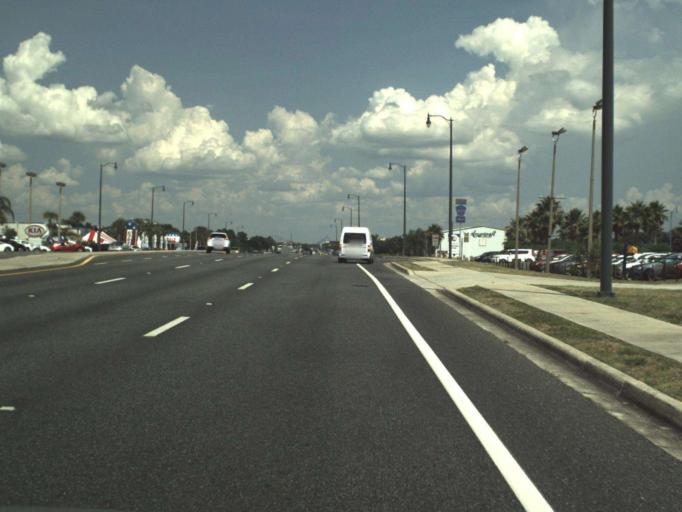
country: US
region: Florida
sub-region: Lake County
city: Silver Lake
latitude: 28.8292
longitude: -81.8077
